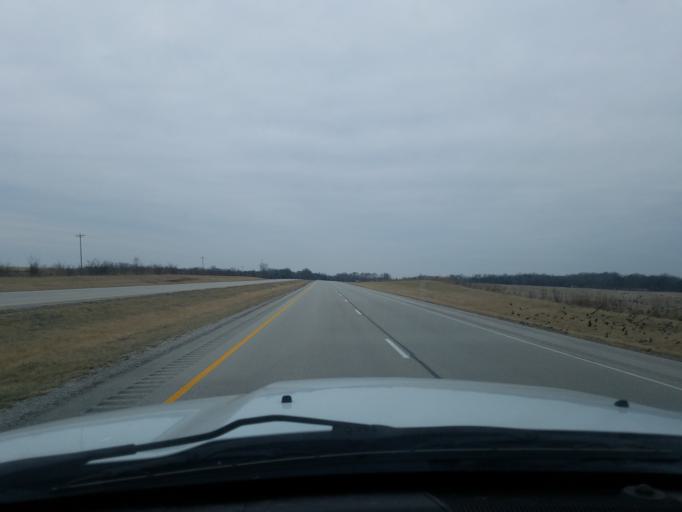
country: US
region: Kentucky
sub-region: Logan County
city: Auburn
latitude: 36.8948
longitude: -86.6026
